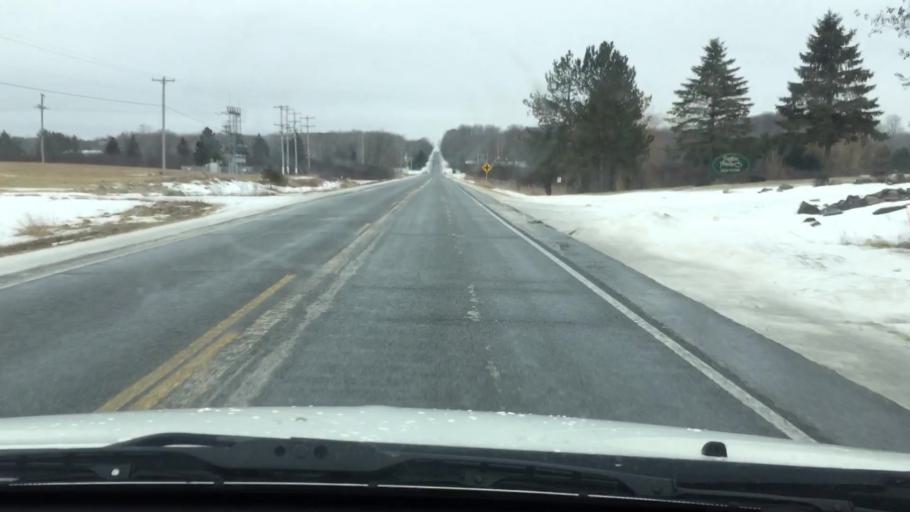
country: US
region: Michigan
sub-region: Wexford County
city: Cadillac
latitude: 44.1061
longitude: -85.4442
